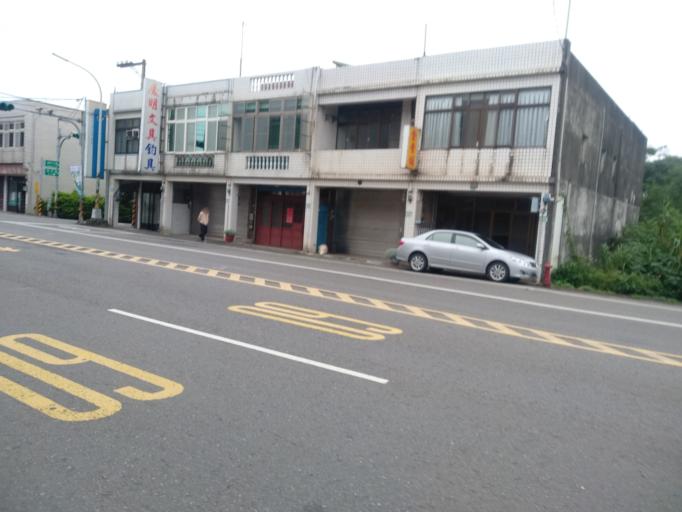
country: TW
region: Taiwan
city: Taoyuan City
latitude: 24.9972
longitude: 121.1618
